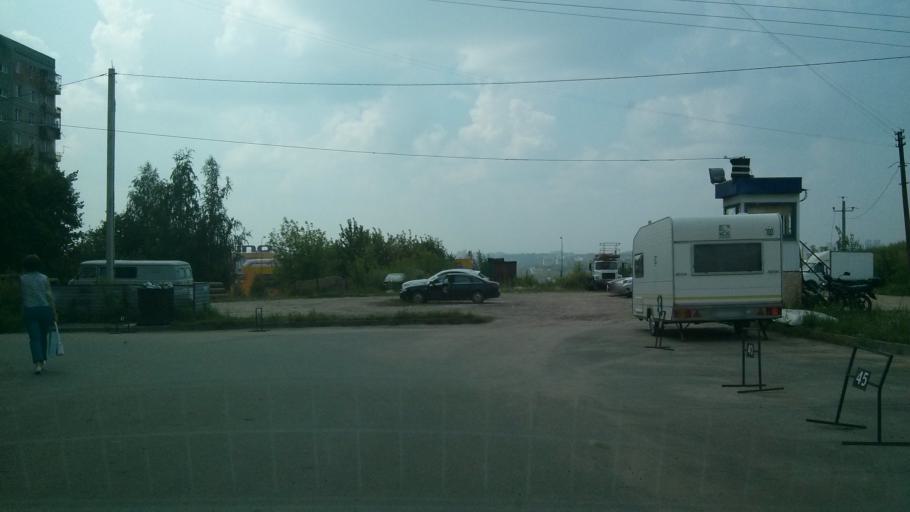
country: RU
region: Nizjnij Novgorod
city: Afonino
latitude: 56.2895
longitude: 44.0705
